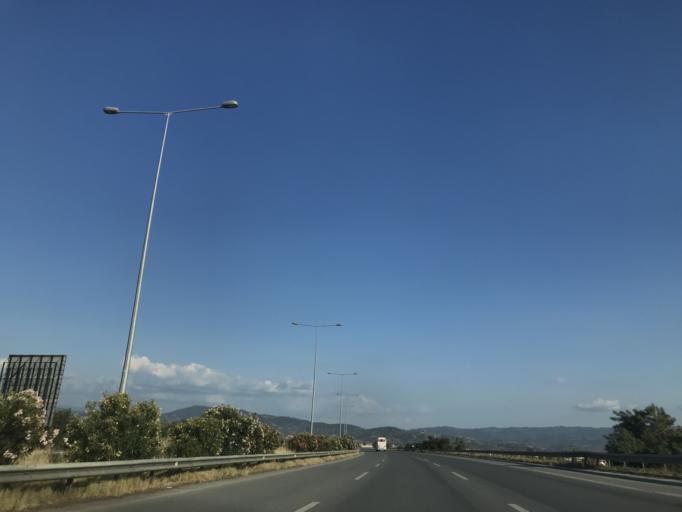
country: TR
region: Aydin
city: Aydin
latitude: 37.8281
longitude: 27.8117
